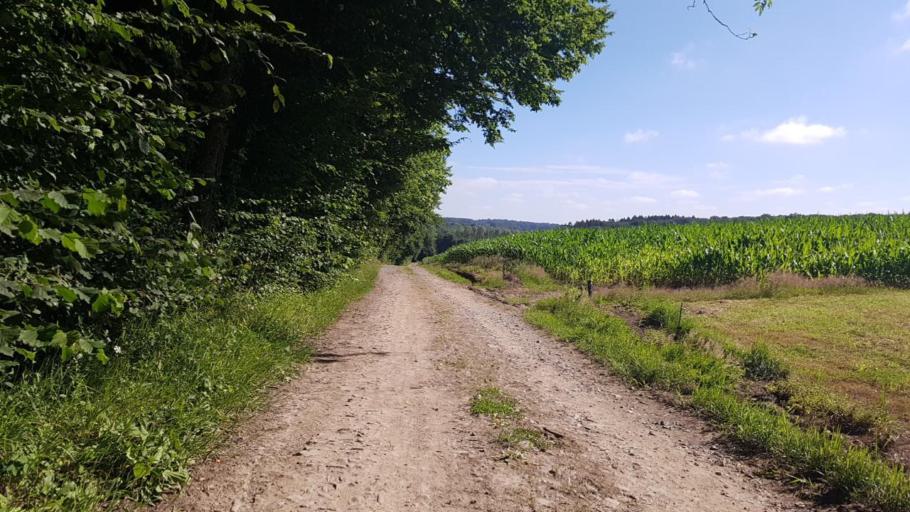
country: FR
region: Nord-Pas-de-Calais
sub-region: Departement du Nord
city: Anor
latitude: 49.9692
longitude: 4.1171
